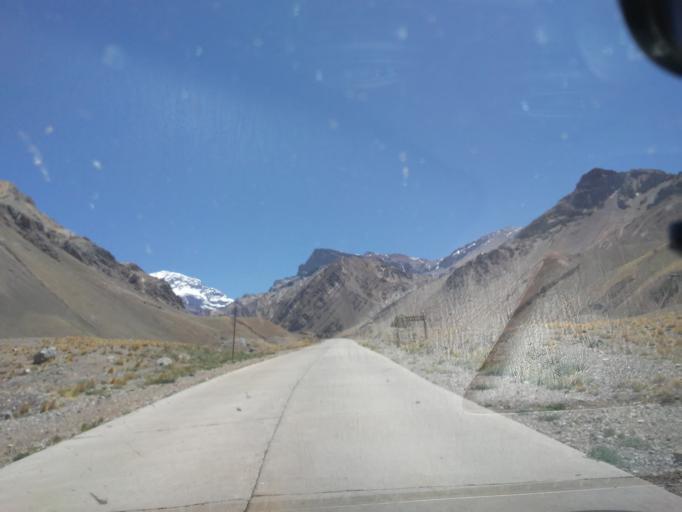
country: CL
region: Valparaiso
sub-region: Provincia de Los Andes
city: Los Andes
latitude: -32.8202
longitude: -69.9422
